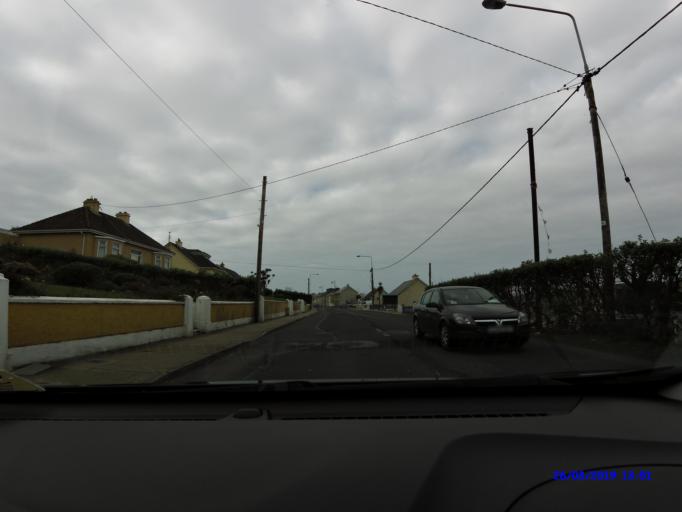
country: IE
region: Connaught
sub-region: Maigh Eo
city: Belmullet
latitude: 54.2217
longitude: -9.9811
